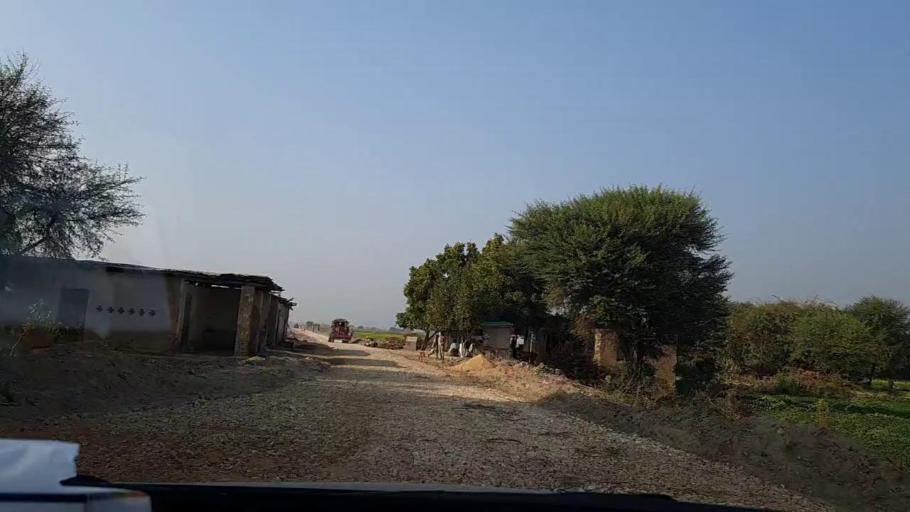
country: PK
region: Sindh
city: Tando Ghulam Ali
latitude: 25.1921
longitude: 68.8779
